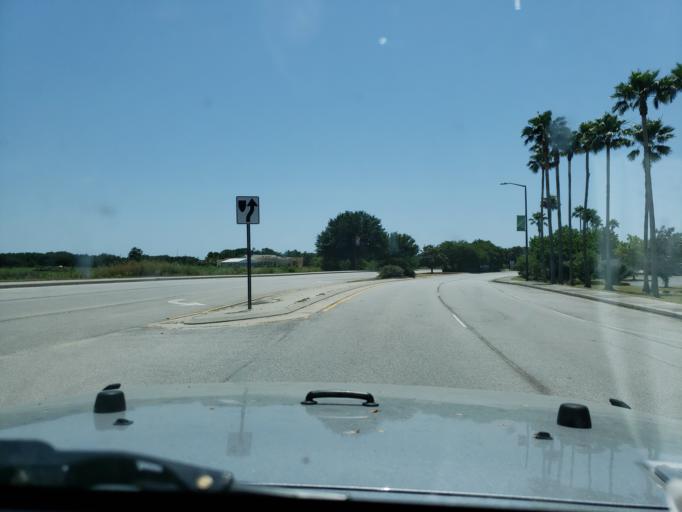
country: US
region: Georgia
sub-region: Chatham County
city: Savannah
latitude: 32.0883
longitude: -81.0862
